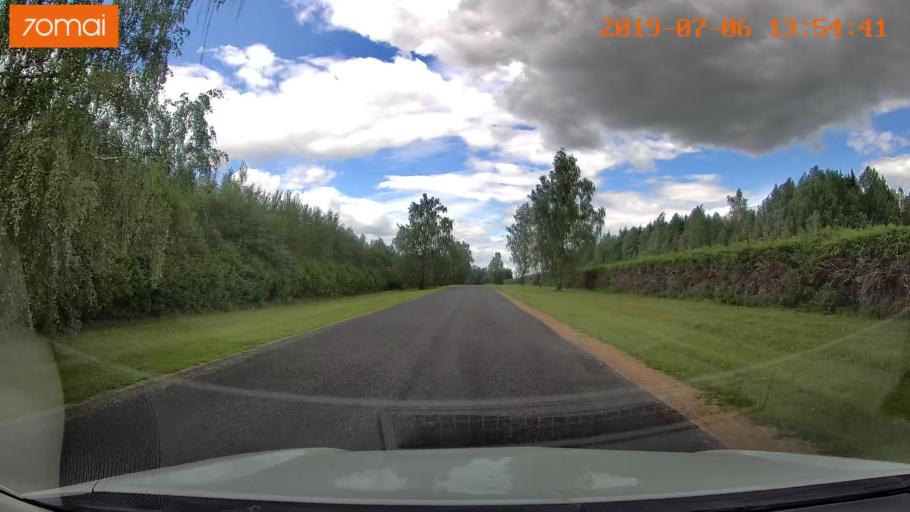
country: BY
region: Minsk
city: Ivyanyets
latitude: 53.7482
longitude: 26.8177
